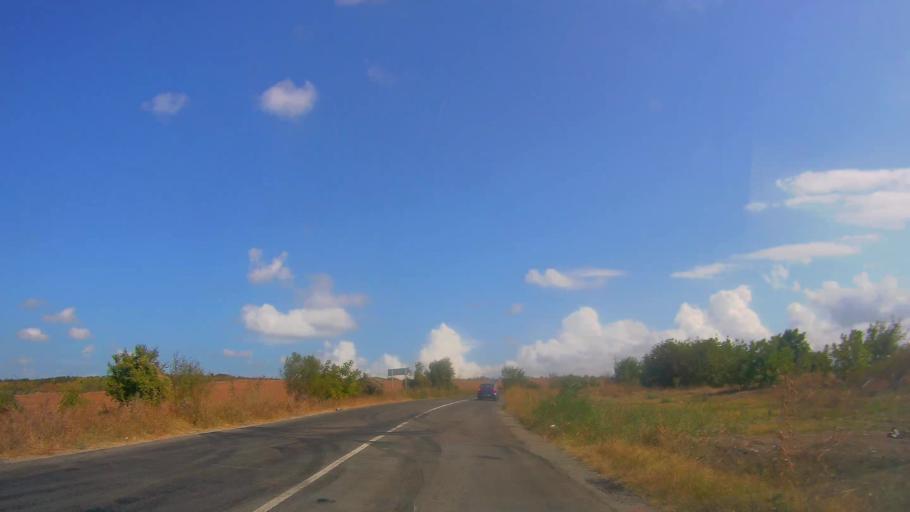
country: BG
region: Burgas
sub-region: Obshtina Burgas
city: Burgas
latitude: 42.4808
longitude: 27.3865
